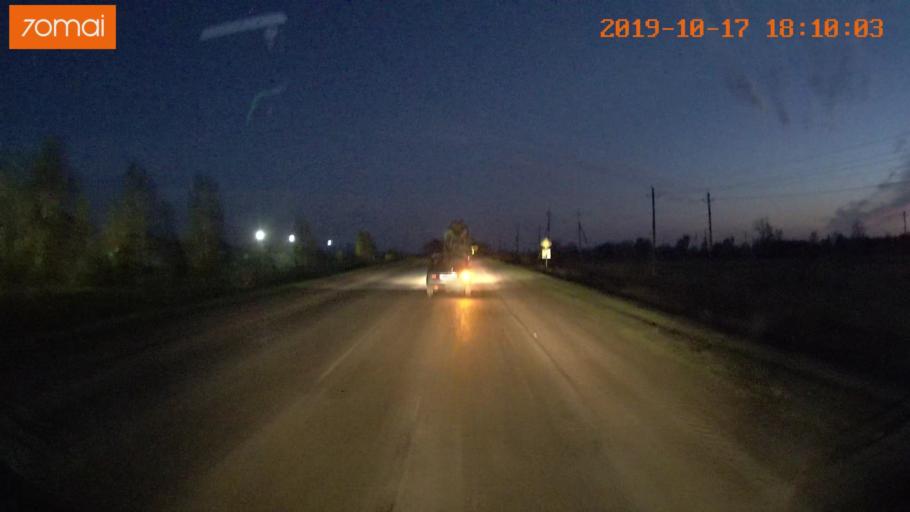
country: RU
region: Tula
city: Kurkino
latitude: 53.4214
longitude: 38.6455
